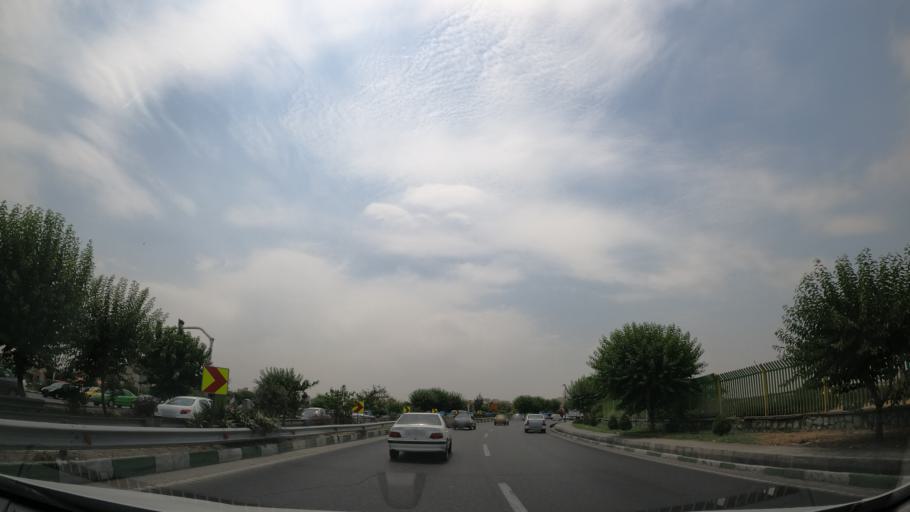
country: IR
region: Tehran
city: Tehran
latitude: 35.6811
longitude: 51.3421
